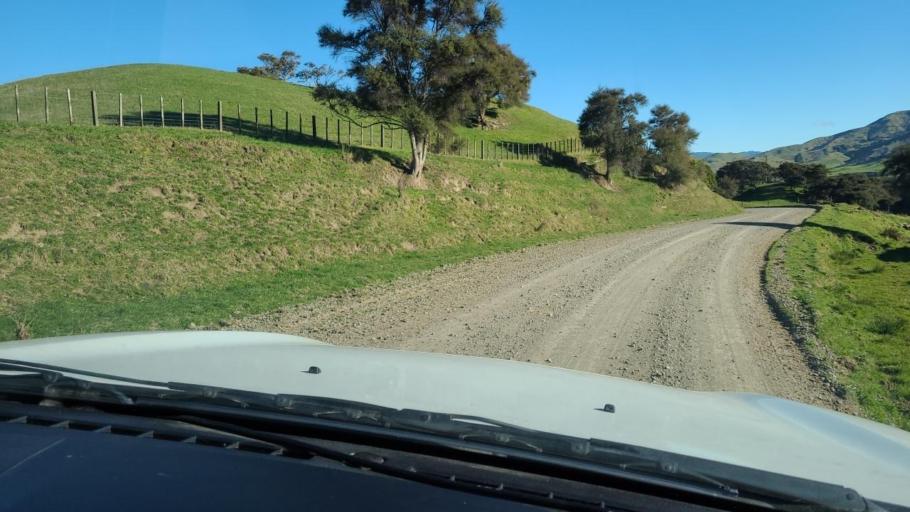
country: NZ
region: Hawke's Bay
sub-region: Napier City
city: Taradale
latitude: -39.5276
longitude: 176.4159
